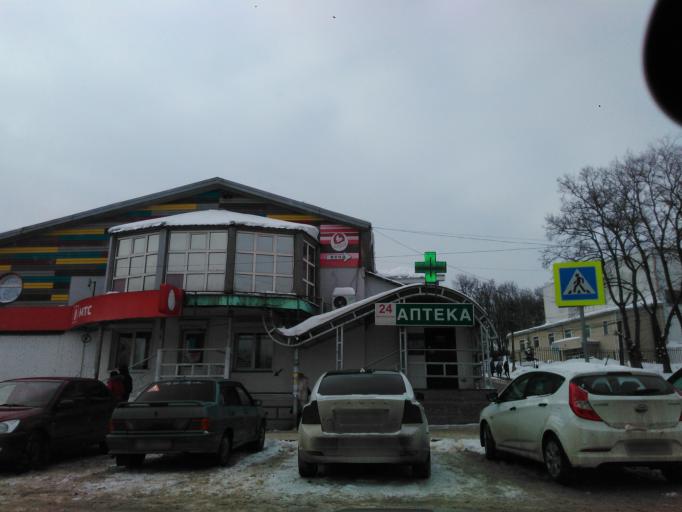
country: RU
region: Moskovskaya
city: Yakhroma
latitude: 56.2901
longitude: 37.4837
